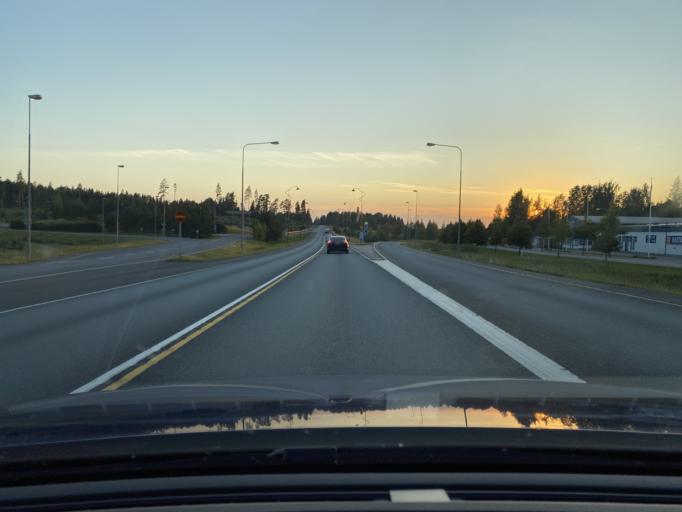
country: FI
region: Pirkanmaa
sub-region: Luoteis-Pirkanmaa
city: Ikaalinen
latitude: 61.7527
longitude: 23.0725
